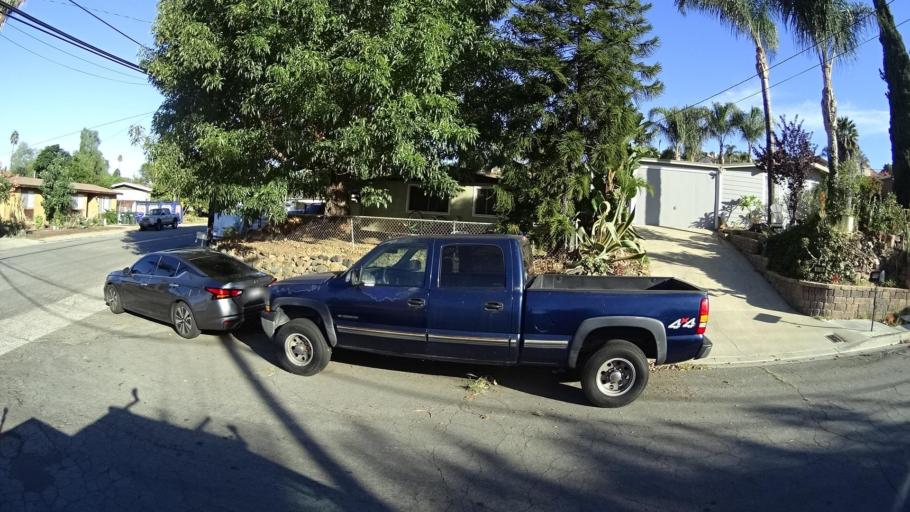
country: US
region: California
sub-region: San Diego County
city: La Presa
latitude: 32.7108
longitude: -116.9886
